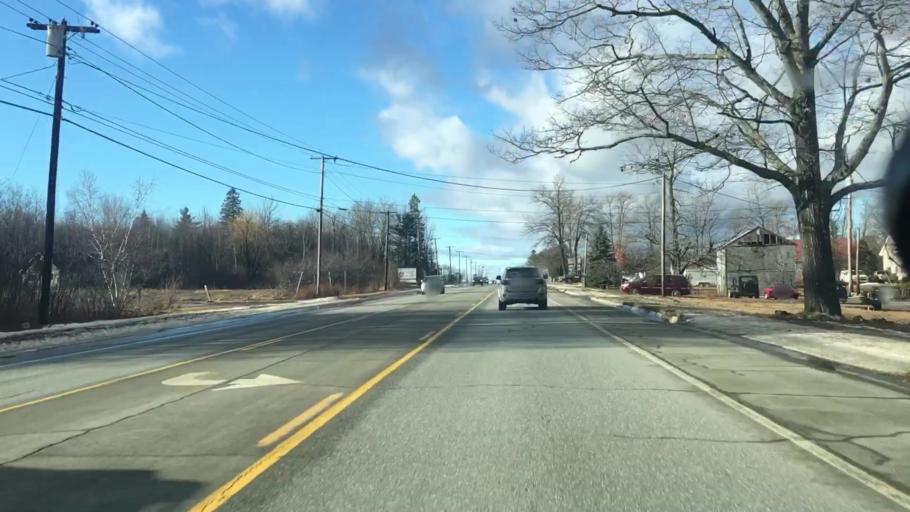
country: US
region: Maine
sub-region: Penobscot County
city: Holden
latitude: 44.7624
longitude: -68.7004
